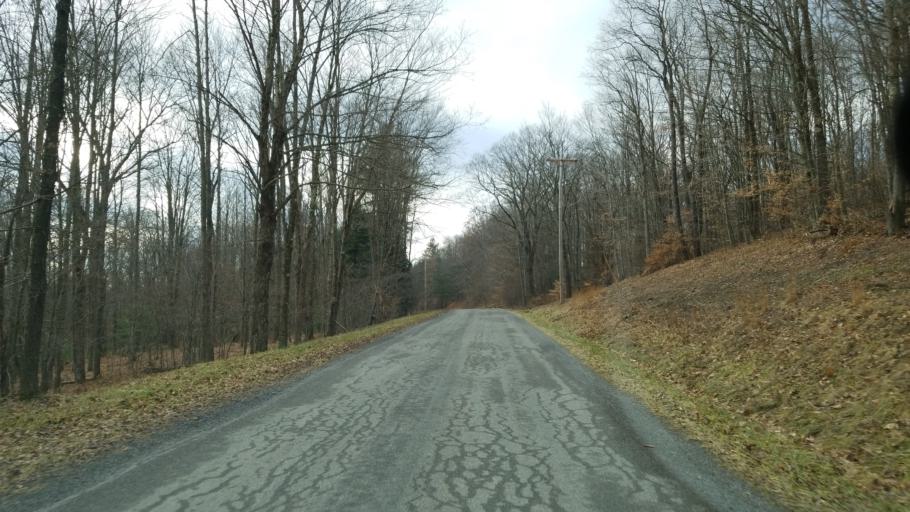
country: US
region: Pennsylvania
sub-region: Clearfield County
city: Treasure Lake
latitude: 41.1299
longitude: -78.6067
